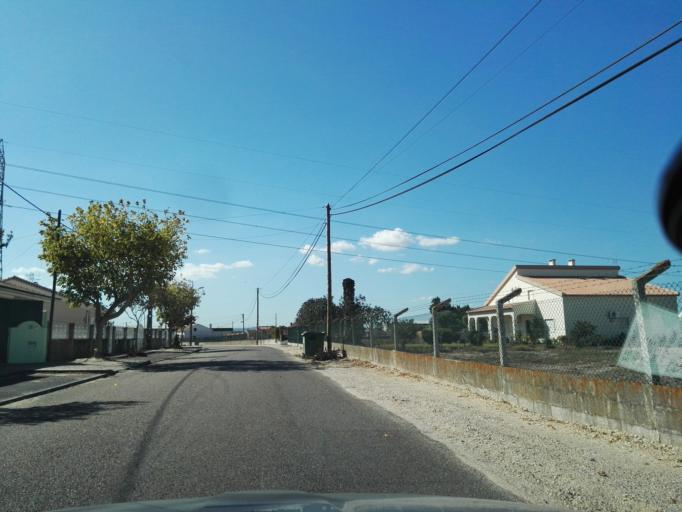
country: PT
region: Santarem
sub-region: Benavente
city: Samora Correia
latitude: 38.9116
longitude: -8.8777
